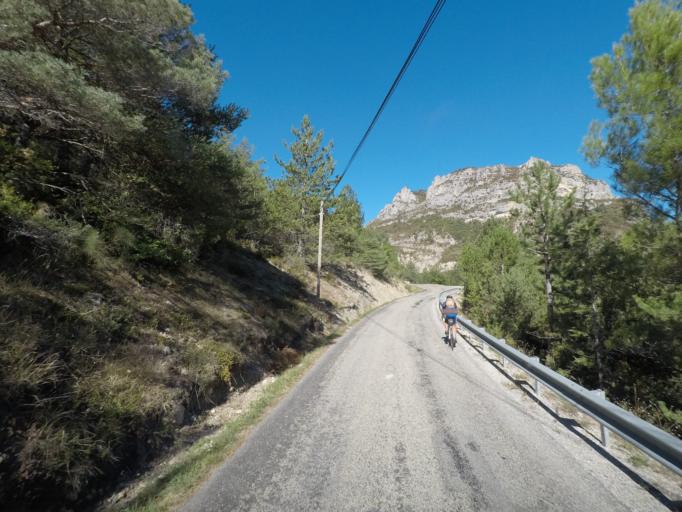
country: FR
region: Rhone-Alpes
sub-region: Departement de la Drome
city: Buis-les-Baronnies
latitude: 44.5036
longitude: 5.3490
